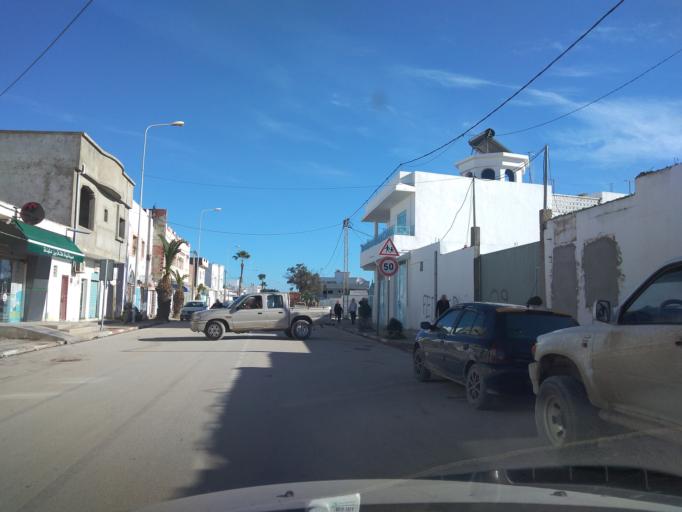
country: TN
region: Ariana
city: Qal'at al Andalus
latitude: 37.0625
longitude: 10.1197
